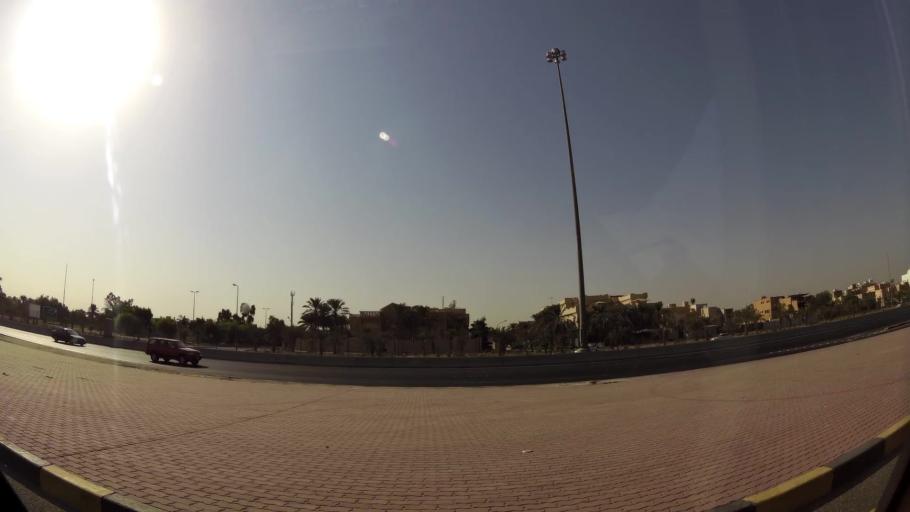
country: KW
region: Al Asimah
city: Ash Shamiyah
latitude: 29.3593
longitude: 47.9679
